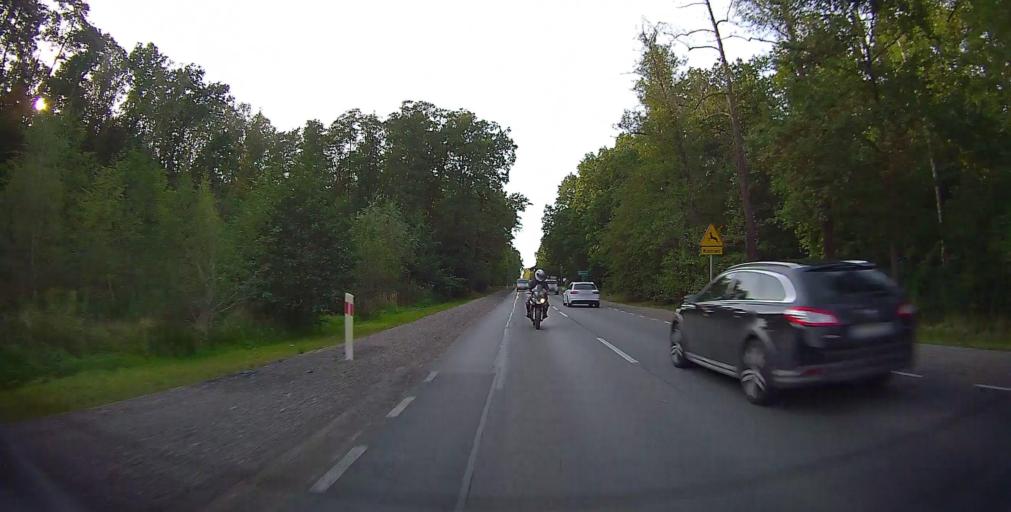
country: PL
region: Masovian Voivodeship
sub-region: Powiat piaseczynski
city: Zabieniec
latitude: 52.0498
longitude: 21.0669
